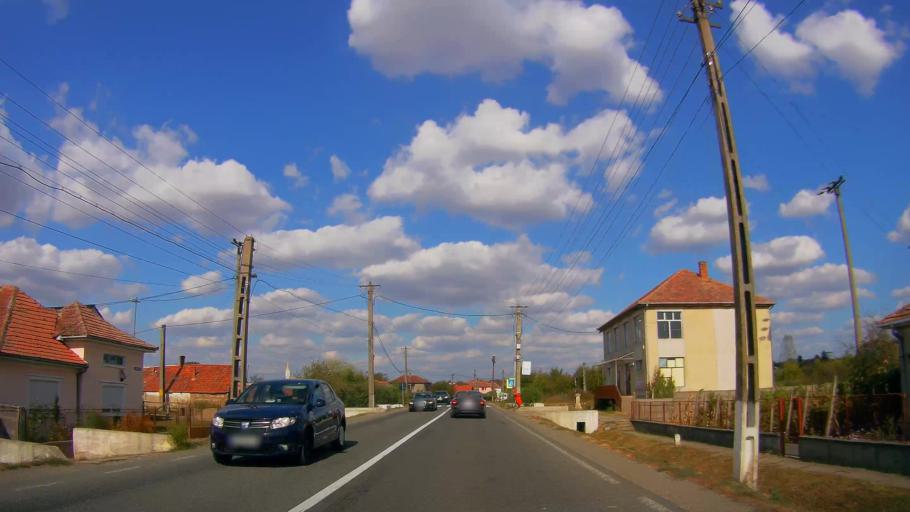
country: RO
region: Satu Mare
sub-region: Oras Ardud
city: Ardud
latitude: 47.6307
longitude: 22.8812
